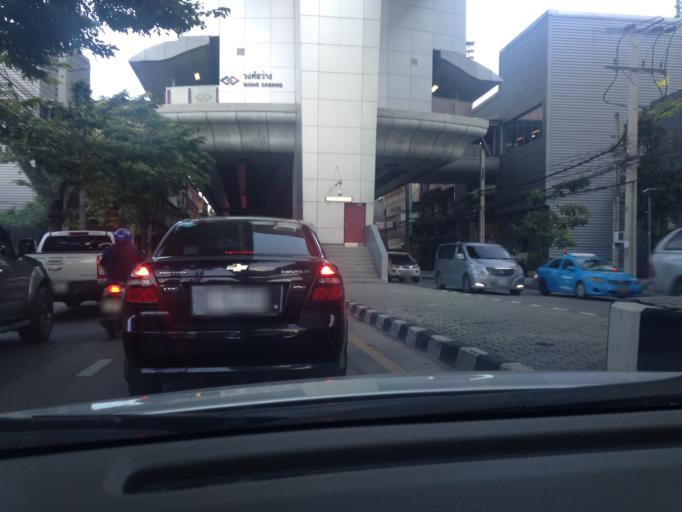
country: TH
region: Bangkok
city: Bang Sue
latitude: 13.8307
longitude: 100.5257
